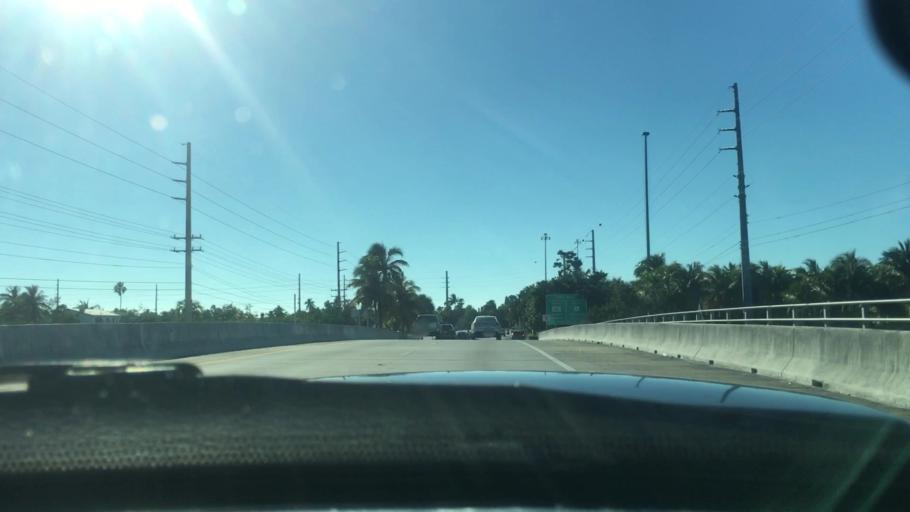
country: US
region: Florida
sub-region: Monroe County
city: Stock Island
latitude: 24.5709
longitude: -81.7494
